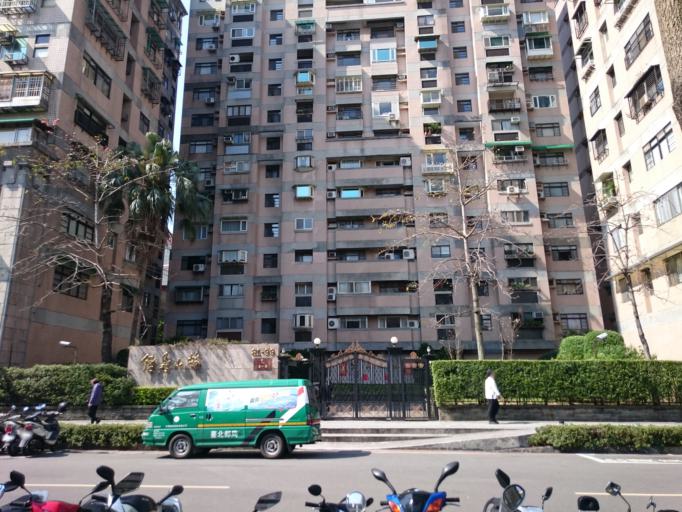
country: TW
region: Taipei
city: Taipei
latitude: 25.0503
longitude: 121.5621
